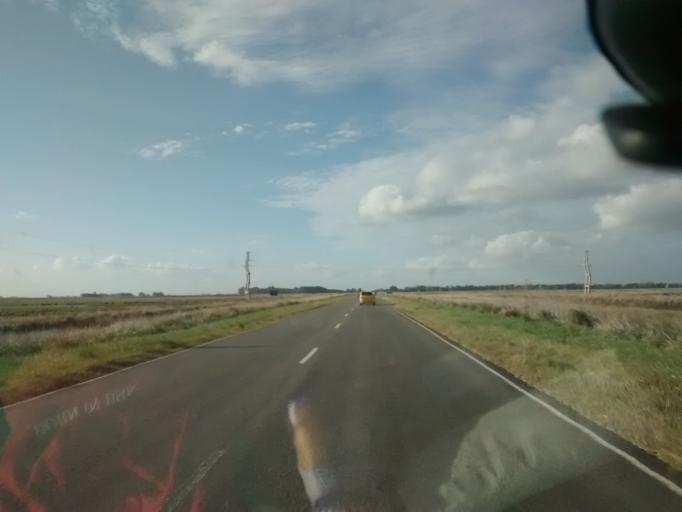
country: AR
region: Buenos Aires
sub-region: Partido de Ayacucho
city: Ayacucho
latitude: -36.6859
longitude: -58.5752
